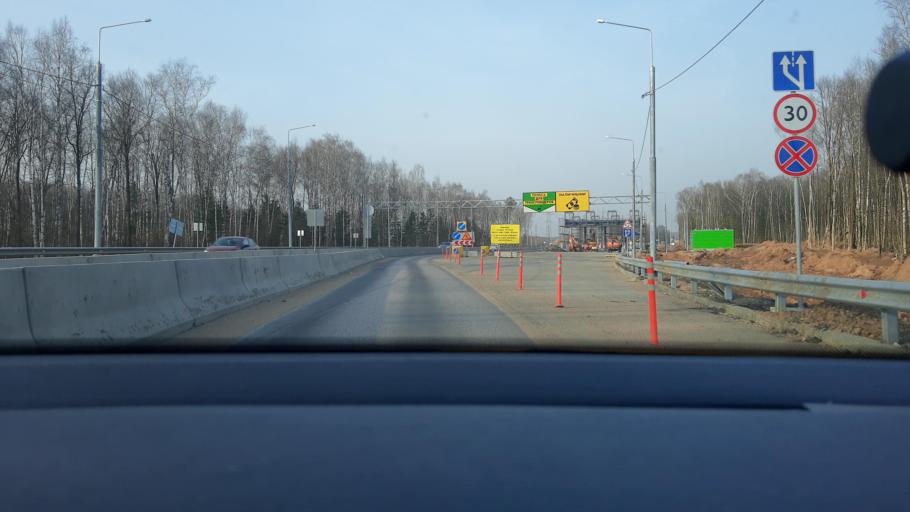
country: RU
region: Moskovskaya
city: Barvikha
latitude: 55.7172
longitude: 37.3125
